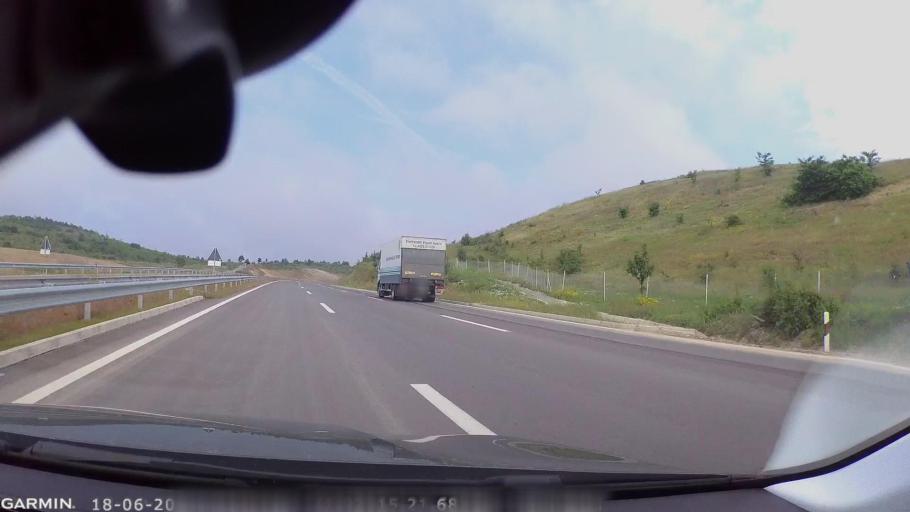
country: MK
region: Petrovec
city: Sredno Konjare
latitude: 41.9448
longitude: 21.7849
